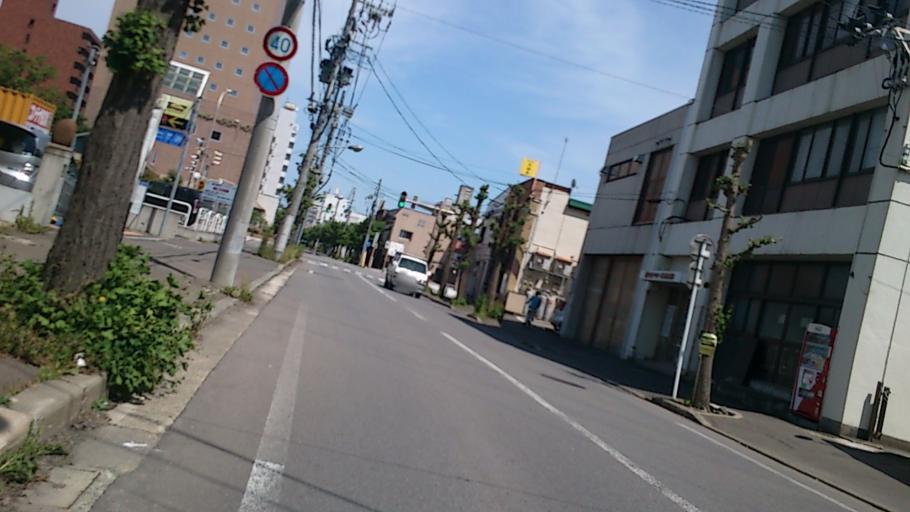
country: JP
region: Aomori
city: Aomori Shi
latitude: 40.8269
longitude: 140.7441
